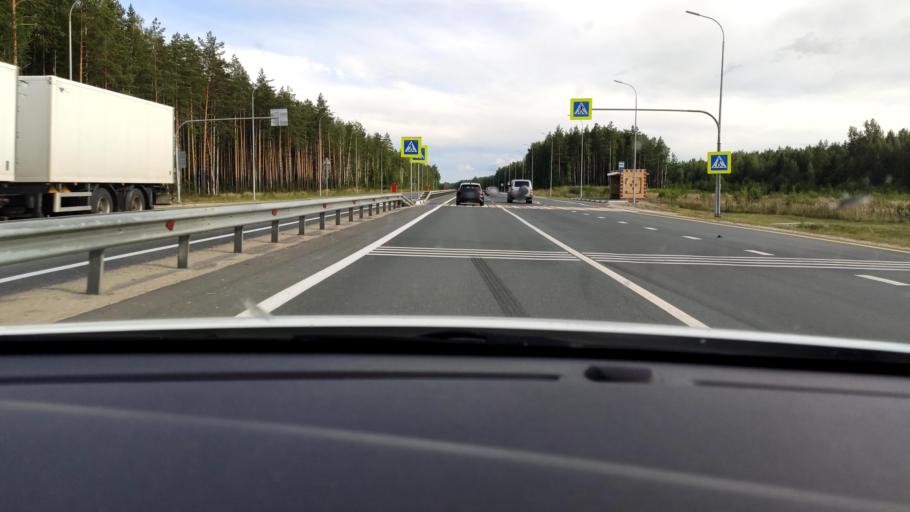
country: RU
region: Mariy-El
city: Surok
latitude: 56.5175
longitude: 48.0149
